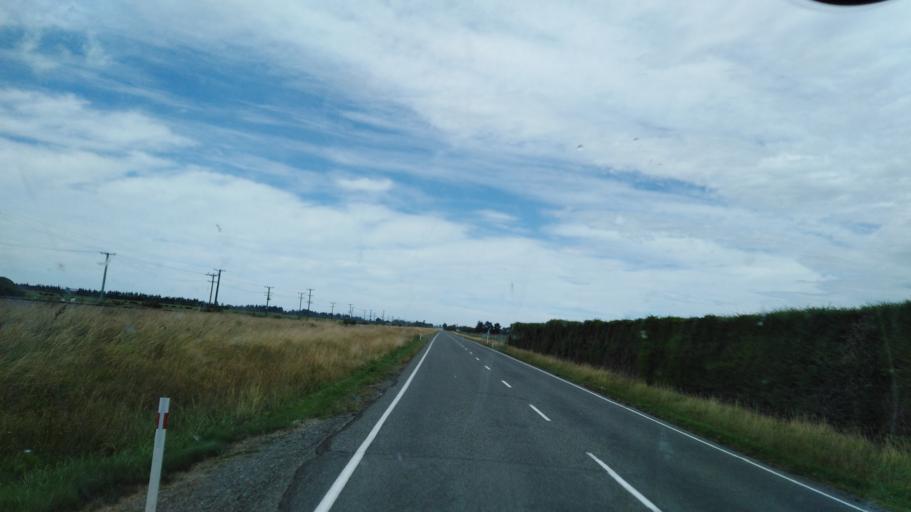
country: NZ
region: Canterbury
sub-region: Selwyn District
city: Darfield
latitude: -43.3594
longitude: 171.9680
